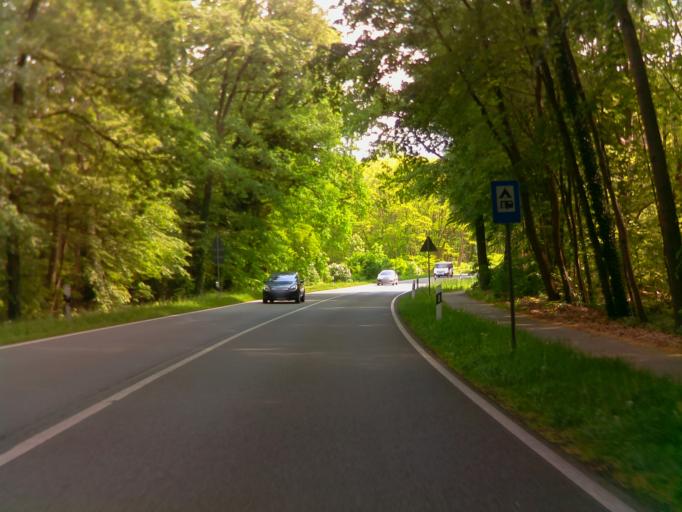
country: DE
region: Brandenburg
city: Nennhausen
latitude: 52.6260
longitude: 12.4537
